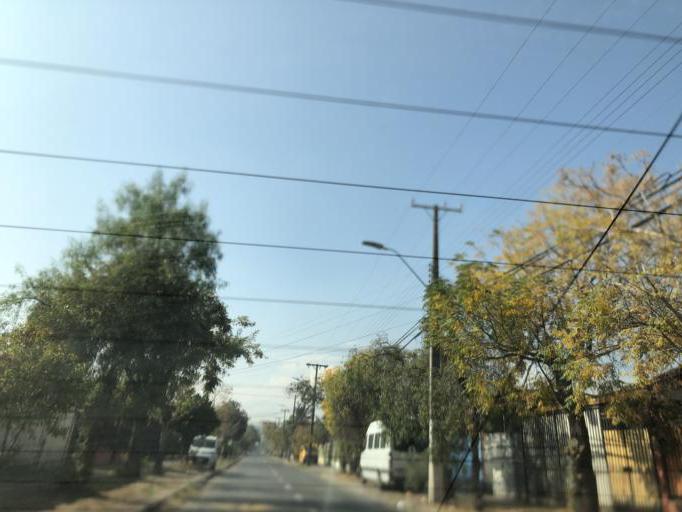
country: CL
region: Santiago Metropolitan
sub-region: Provincia de Cordillera
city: Puente Alto
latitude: -33.6033
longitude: -70.5693
